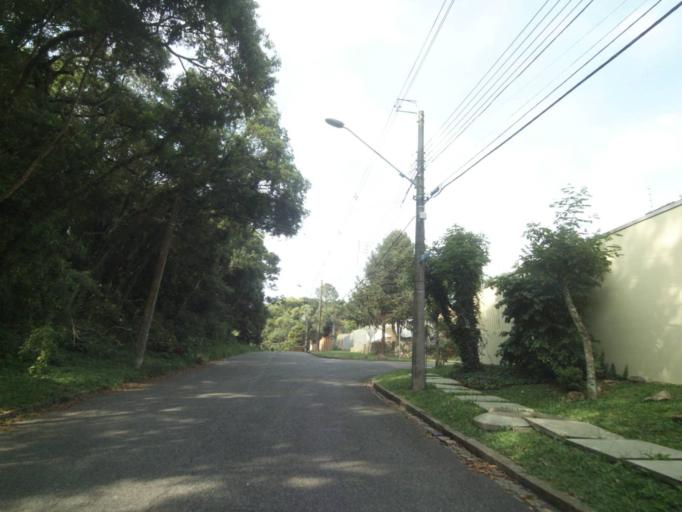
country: BR
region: Parana
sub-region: Curitiba
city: Curitiba
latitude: -25.4109
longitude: -49.3152
